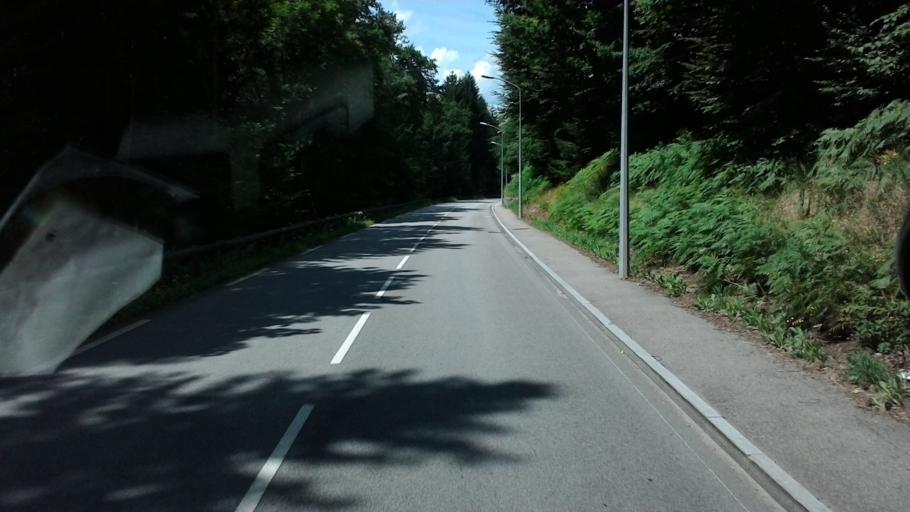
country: FR
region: Lorraine
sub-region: Departement des Vosges
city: Le Tholy
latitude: 48.0846
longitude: 6.7377
